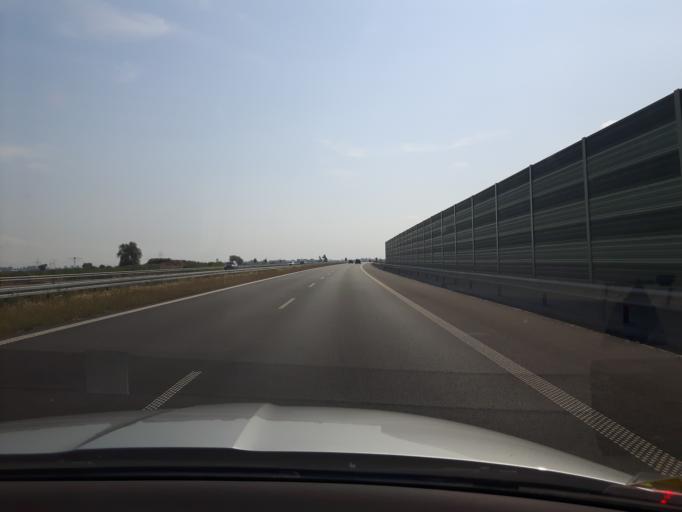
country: PL
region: Pomeranian Voivodeship
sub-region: Powiat nowodworski
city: Ostaszewo
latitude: 54.2511
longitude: 18.9824
